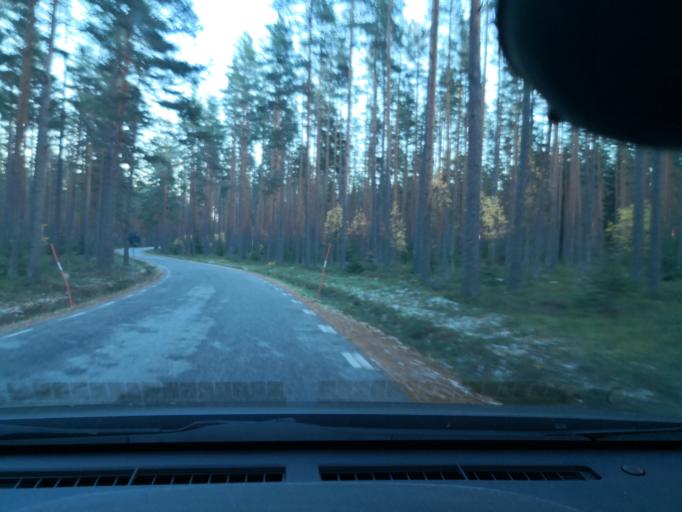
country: SE
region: Vaestmanland
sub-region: Vasteras
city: Tillberga
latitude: 59.7701
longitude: 16.5784
